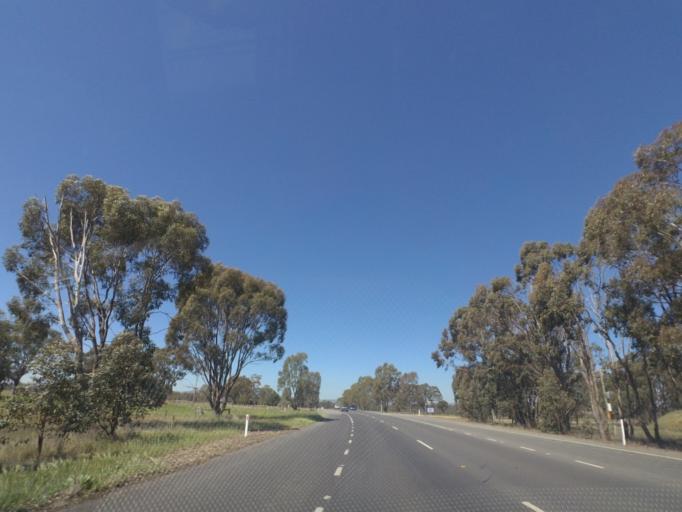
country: AU
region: Victoria
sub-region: Murrindindi
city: Kinglake West
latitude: -37.0298
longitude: 145.0844
